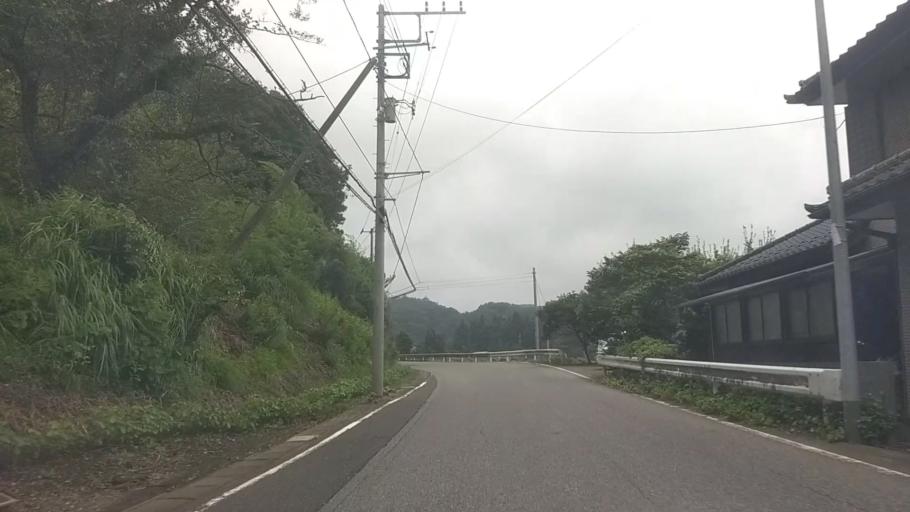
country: JP
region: Chiba
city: Kawaguchi
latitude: 35.2254
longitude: 140.0166
